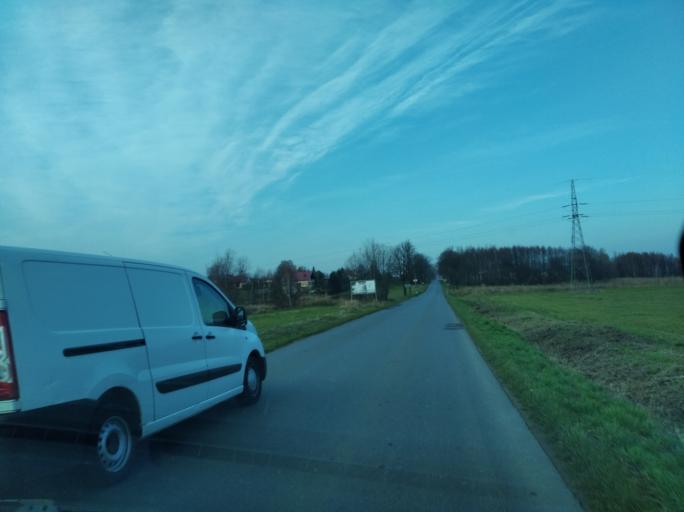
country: PL
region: Subcarpathian Voivodeship
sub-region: Powiat ropczycko-sedziszowski
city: Iwierzyce
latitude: 50.0438
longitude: 21.7453
